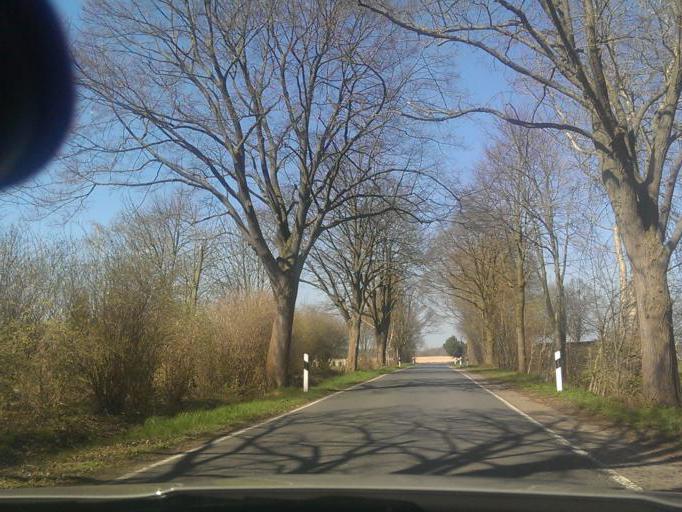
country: DE
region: Lower Saxony
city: Elze
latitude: 52.5414
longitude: 9.7201
